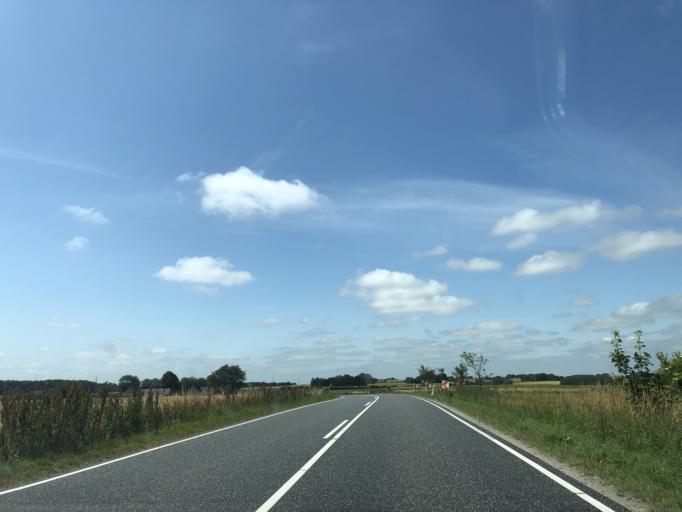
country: DK
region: Central Jutland
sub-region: Randers Kommune
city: Langa
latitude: 56.3382
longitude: 9.8558
